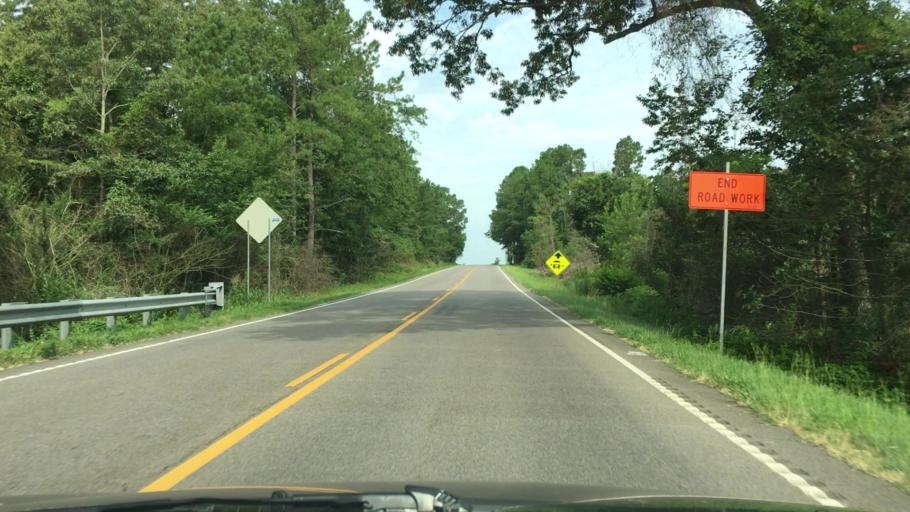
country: US
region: South Carolina
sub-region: Lexington County
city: Leesville
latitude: 33.6870
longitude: -81.4605
